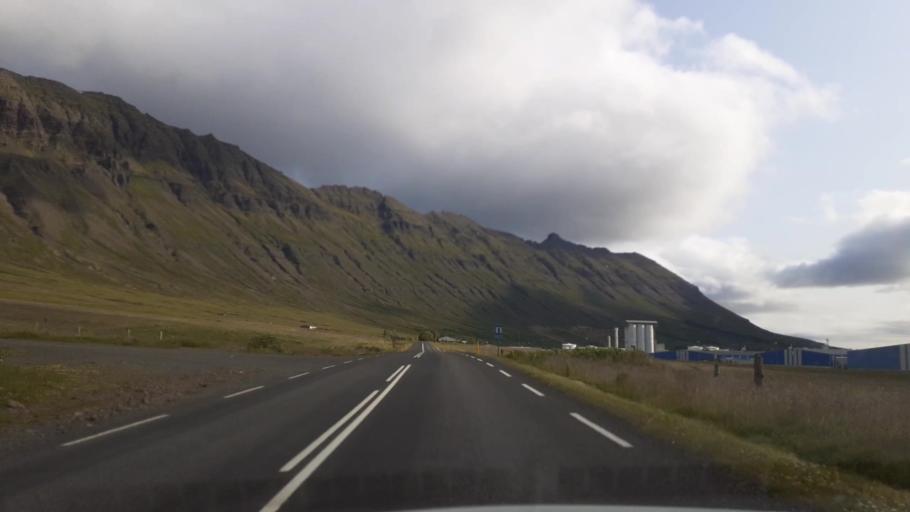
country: IS
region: East
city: Neskaupstadur
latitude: 65.1350
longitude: -13.7506
